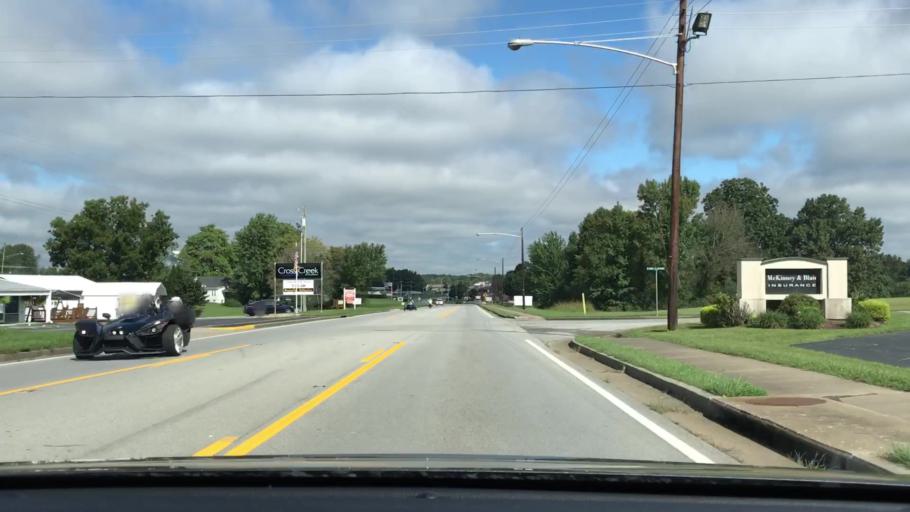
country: US
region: Kentucky
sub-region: Russell County
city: Jamestown
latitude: 37.0062
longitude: -85.0742
